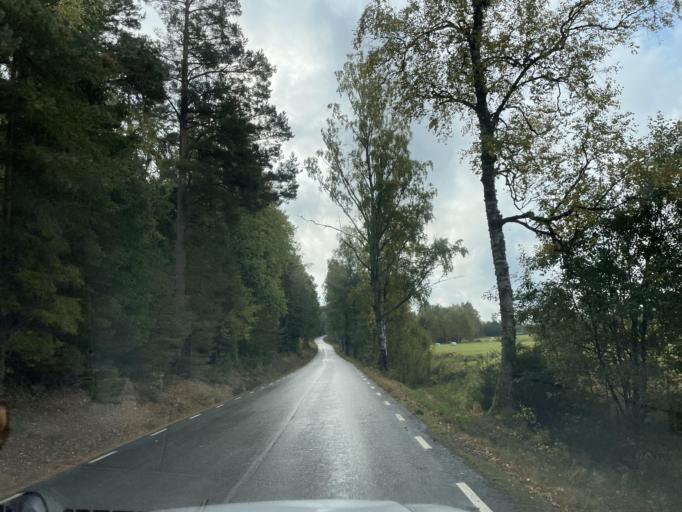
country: SE
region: Vaermland
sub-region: Karlstads Kommun
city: Skattkarr
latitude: 59.4455
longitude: 13.6075
